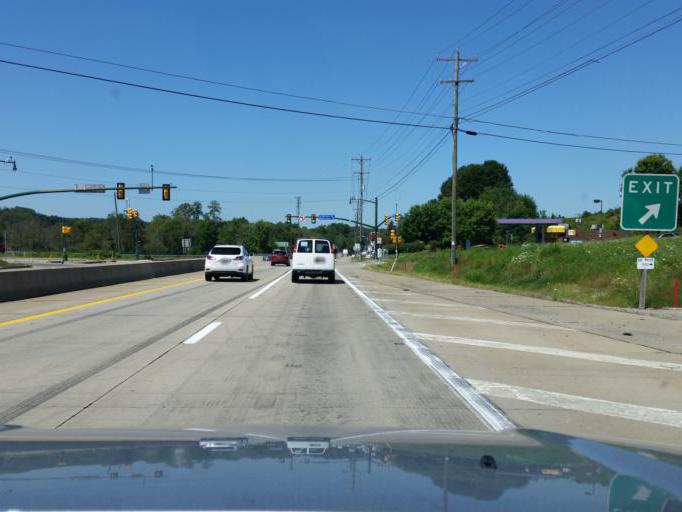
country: US
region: Pennsylvania
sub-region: Westmoreland County
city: Delmont
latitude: 40.4125
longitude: -79.6297
